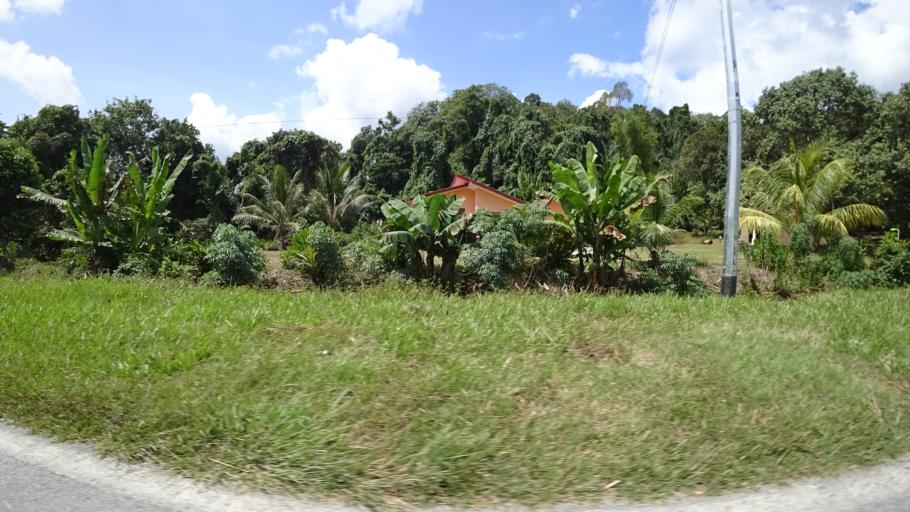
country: BN
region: Tutong
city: Tutong
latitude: 4.6795
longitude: 114.8102
